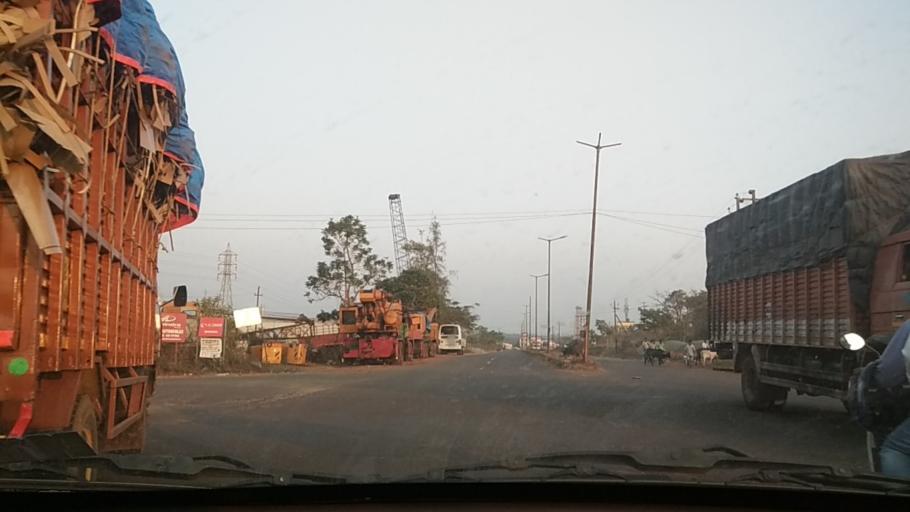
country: IN
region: Goa
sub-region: South Goa
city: Sancoale
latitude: 15.3665
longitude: 73.9469
